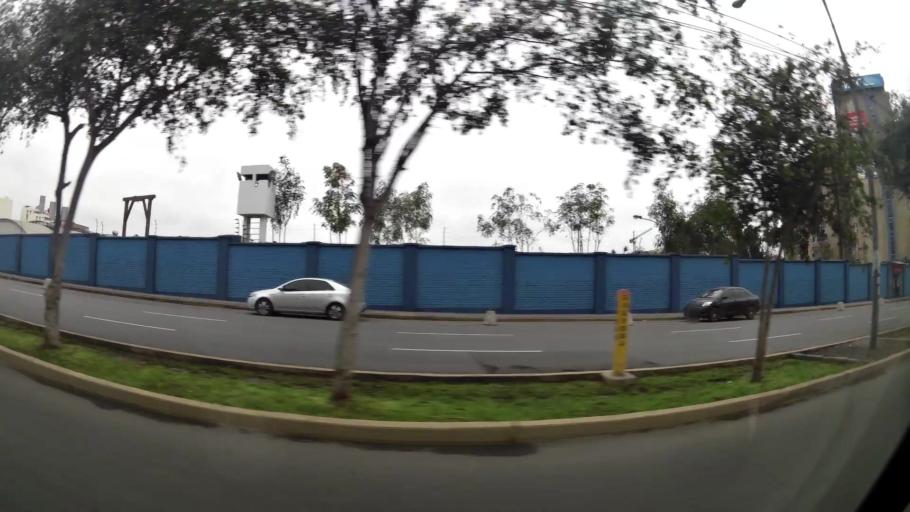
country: PE
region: Lima
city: Lima
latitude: -12.0492
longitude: -77.0549
